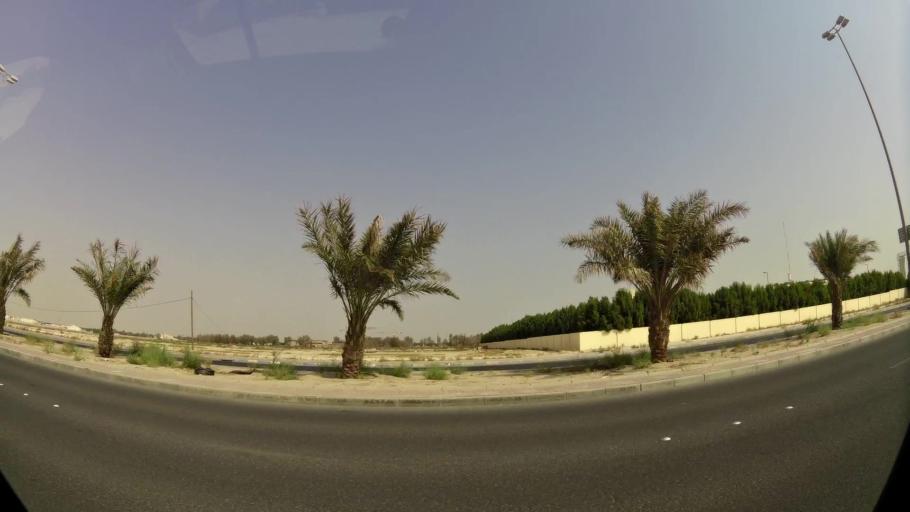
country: KW
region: Muhafazat al Jahra'
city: Al Jahra'
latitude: 29.3238
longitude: 47.7281
